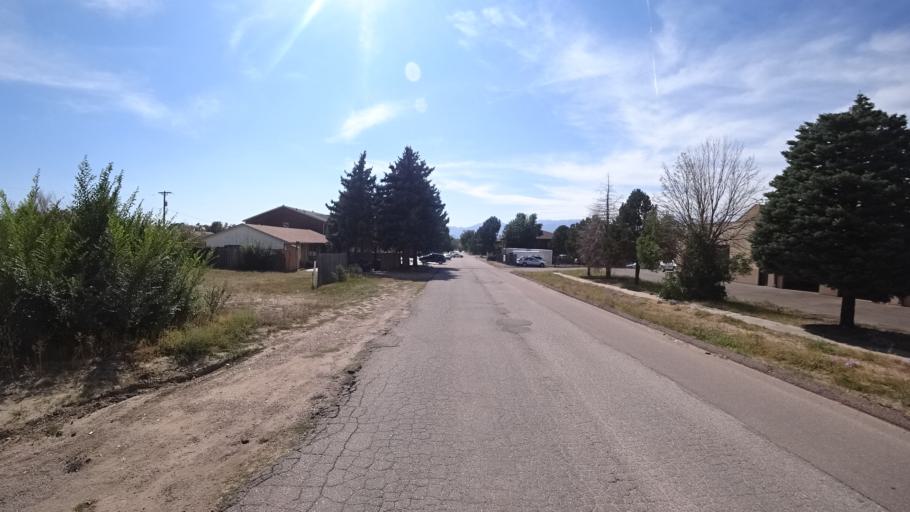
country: US
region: Colorado
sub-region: El Paso County
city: Cimarron Hills
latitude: 38.8946
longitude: -104.7492
